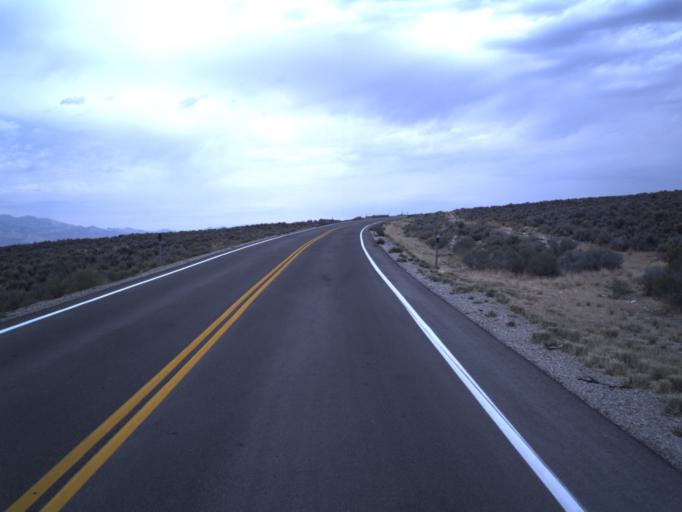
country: US
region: Utah
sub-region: Tooele County
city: Tooele
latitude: 40.2912
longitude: -112.2711
